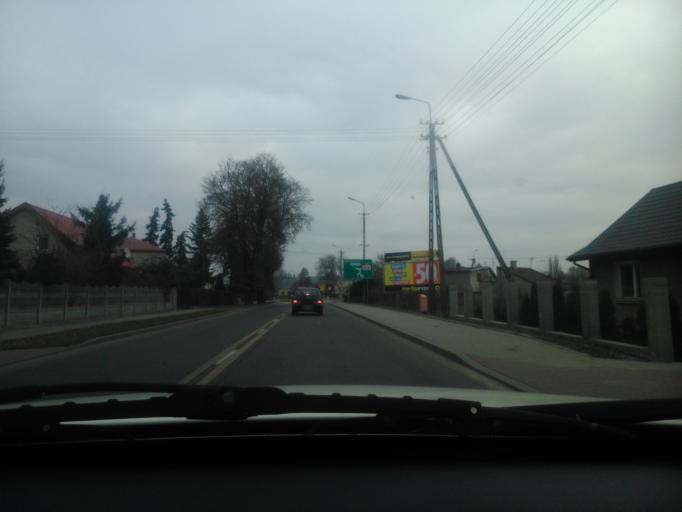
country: PL
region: Masovian Voivodeship
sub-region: Powiat mlawski
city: Mlawa
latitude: 53.1279
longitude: 20.3446
